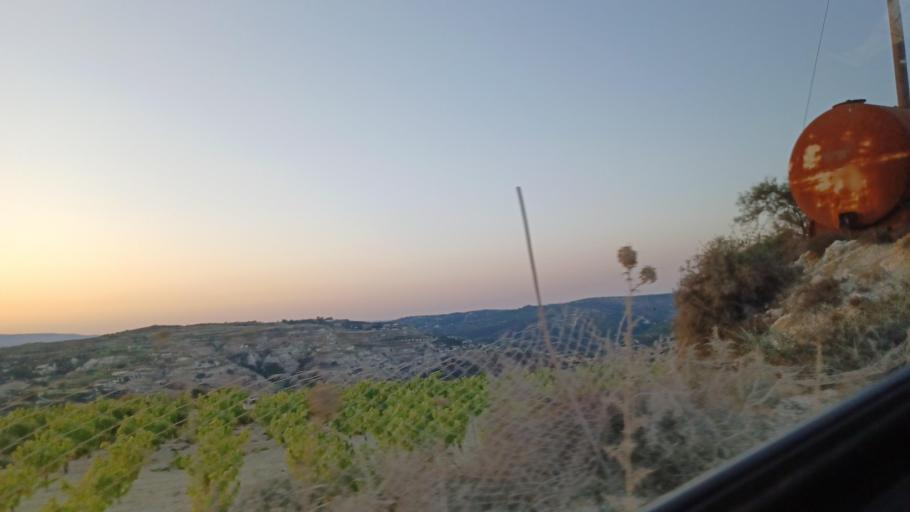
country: CY
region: Pafos
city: Tala
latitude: 34.8937
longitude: 32.4441
